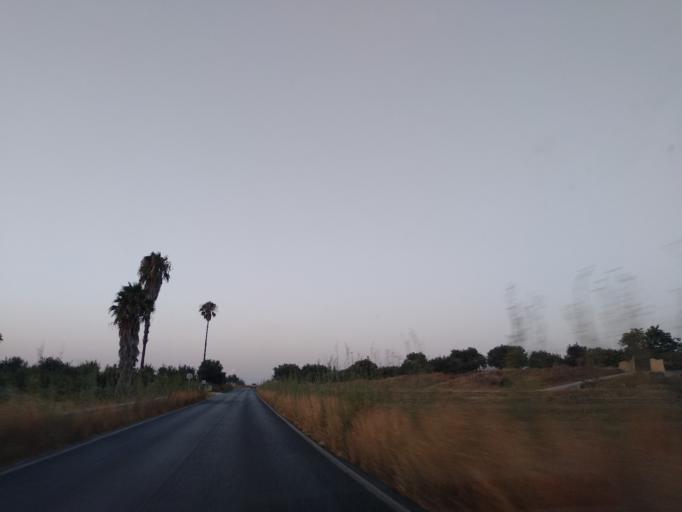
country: ES
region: Andalusia
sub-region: Provincia de Malaga
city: Alhaurin el Grande
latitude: 36.6671
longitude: -4.6679
